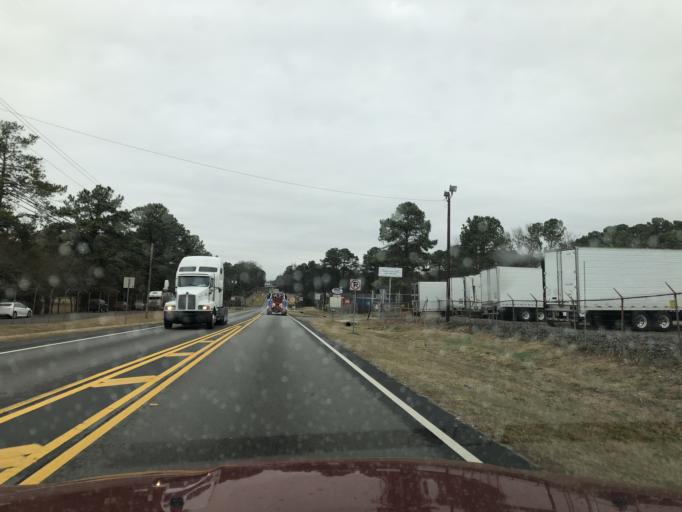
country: US
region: Georgia
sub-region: Clayton County
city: Lake City
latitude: 33.6204
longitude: -84.3090
